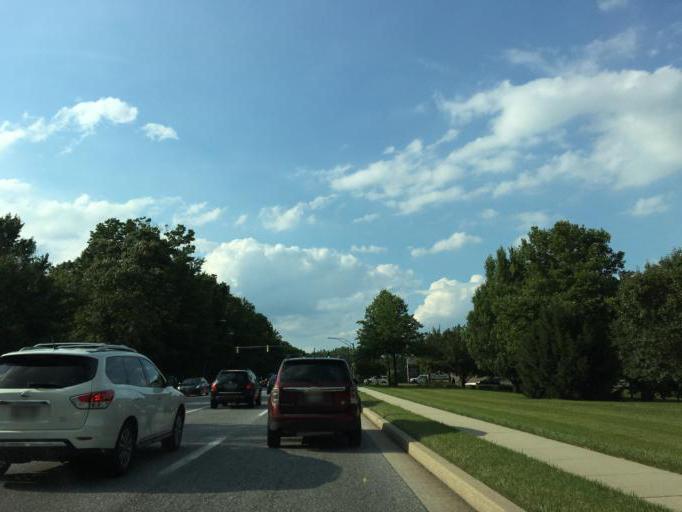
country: US
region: Maryland
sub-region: Baltimore County
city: White Marsh
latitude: 39.3826
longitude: -76.4601
